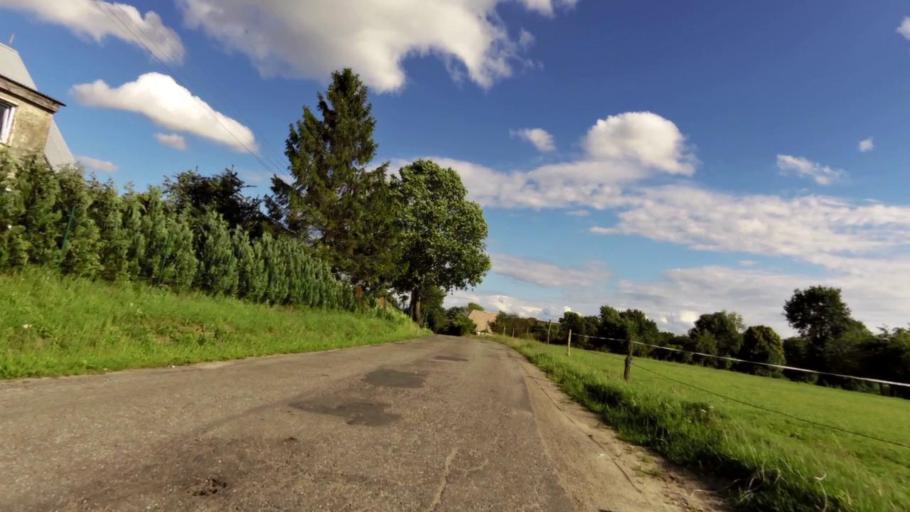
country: PL
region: West Pomeranian Voivodeship
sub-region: Powiat slawienski
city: Slawno
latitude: 54.4334
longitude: 16.7691
